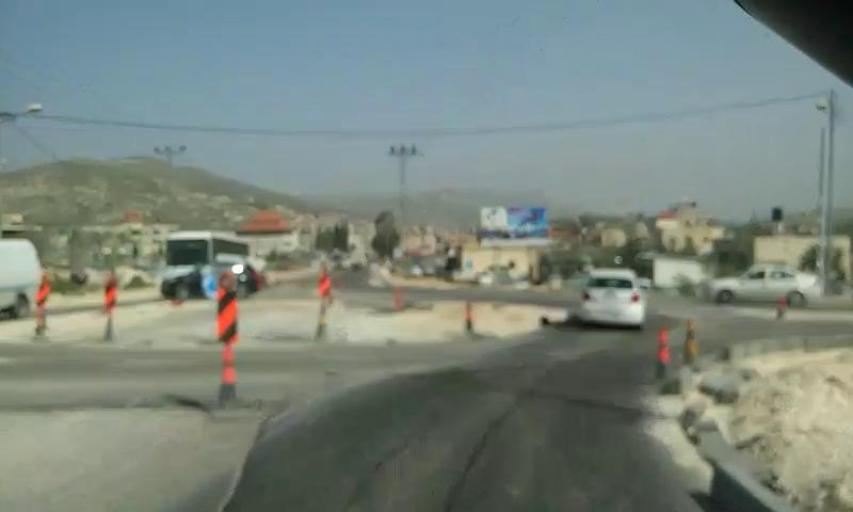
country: PS
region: West Bank
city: Huwwarah
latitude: 32.1371
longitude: 35.2581
